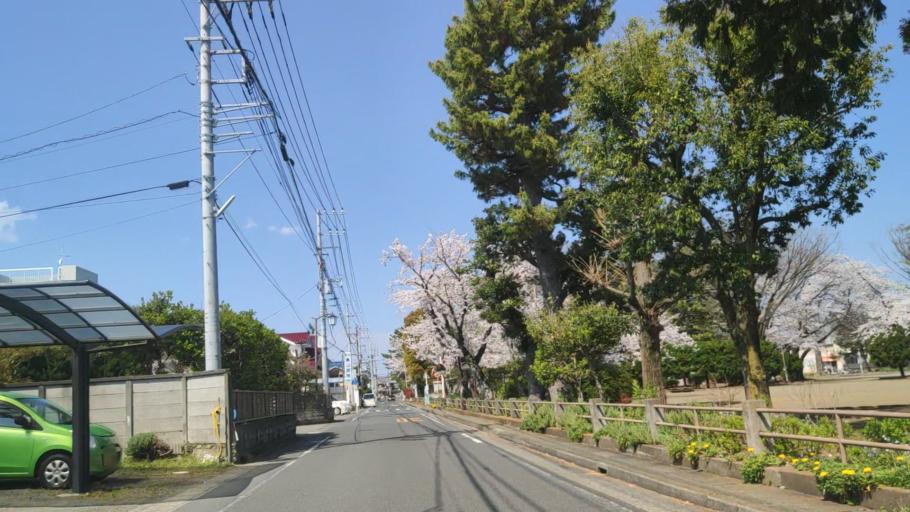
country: JP
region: Kanagawa
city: Hiratsuka
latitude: 35.3349
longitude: 139.3311
